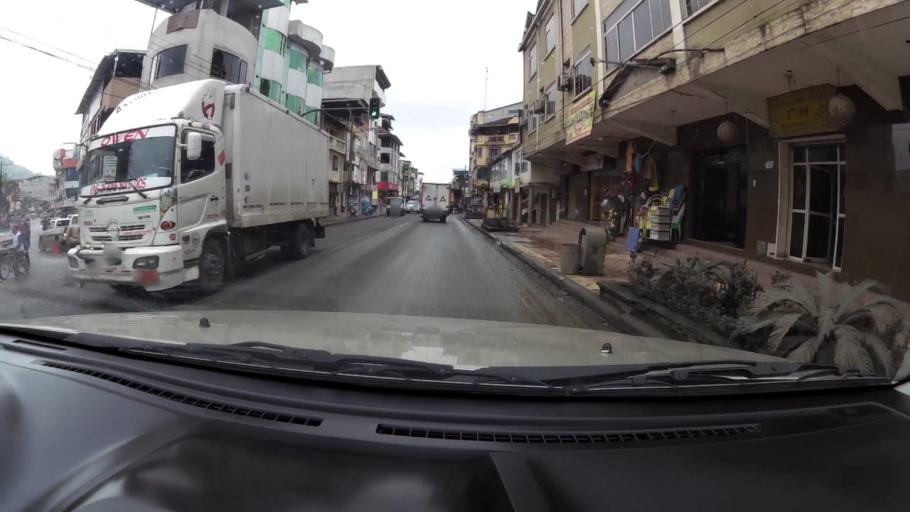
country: EC
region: Guayas
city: Balao
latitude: -3.0612
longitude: -79.7470
